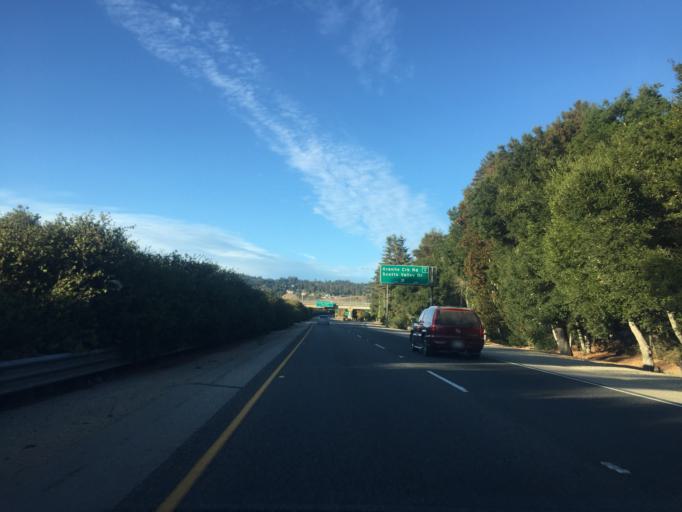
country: US
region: California
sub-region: Santa Cruz County
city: Scotts Valley
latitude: 37.0590
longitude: -122.0056
